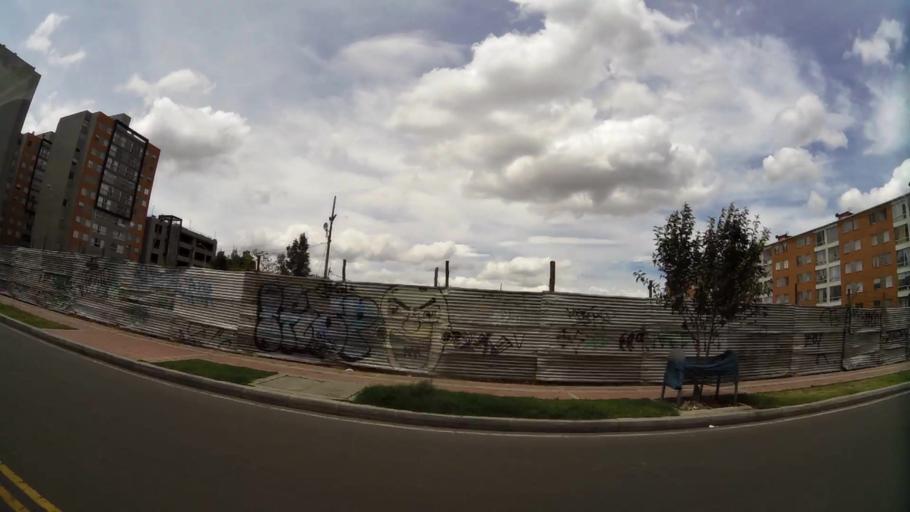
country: CO
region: Cundinamarca
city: Funza
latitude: 4.6538
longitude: -74.1553
